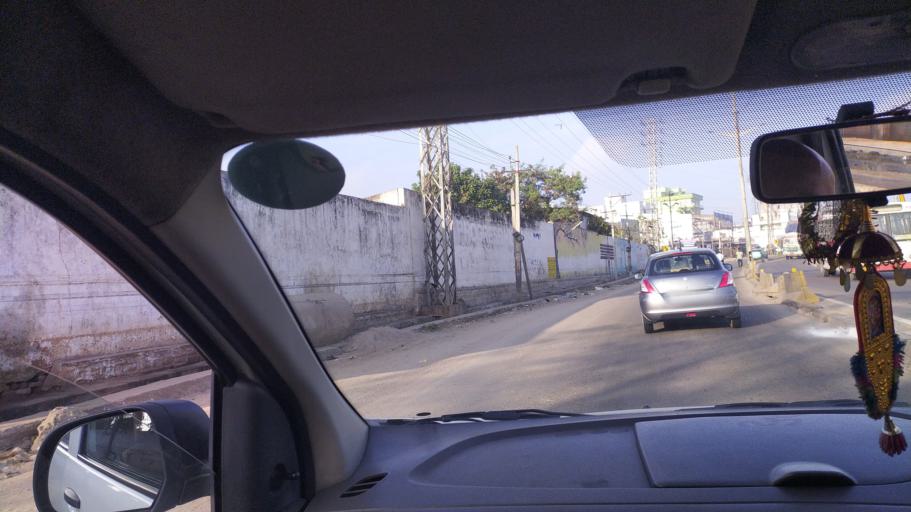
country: IN
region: Telangana
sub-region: Rangareddi
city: Balapur
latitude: 17.3143
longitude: 78.4602
